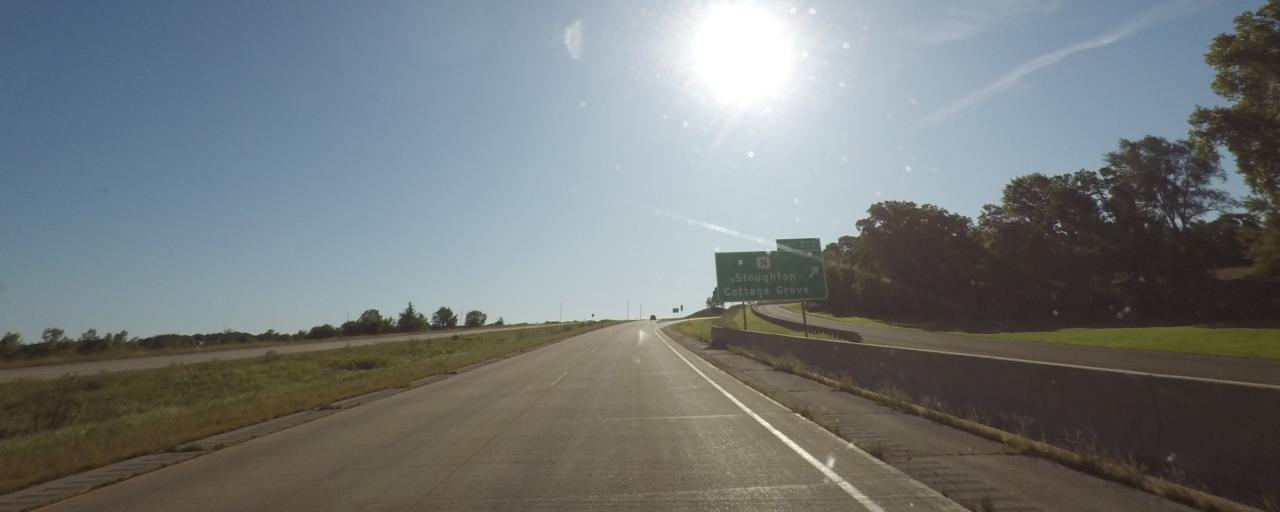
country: US
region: Wisconsin
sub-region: Dane County
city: Cottage Grove
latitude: 43.0328
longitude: -89.2073
